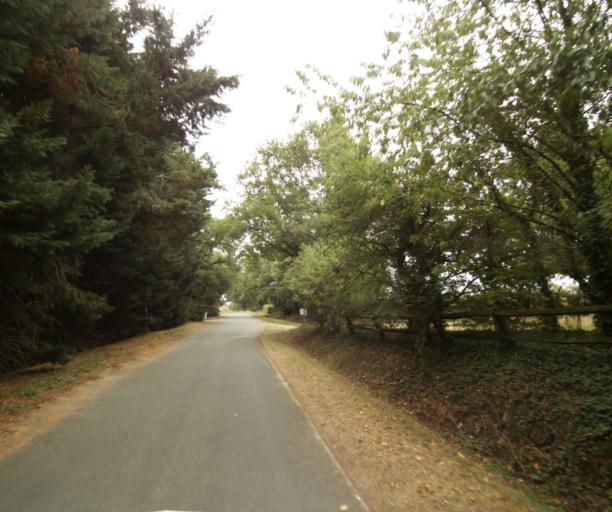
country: FR
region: Pays de la Loire
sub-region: Departement de la Sarthe
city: Sable-sur-Sarthe
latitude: 47.8204
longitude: -0.3657
